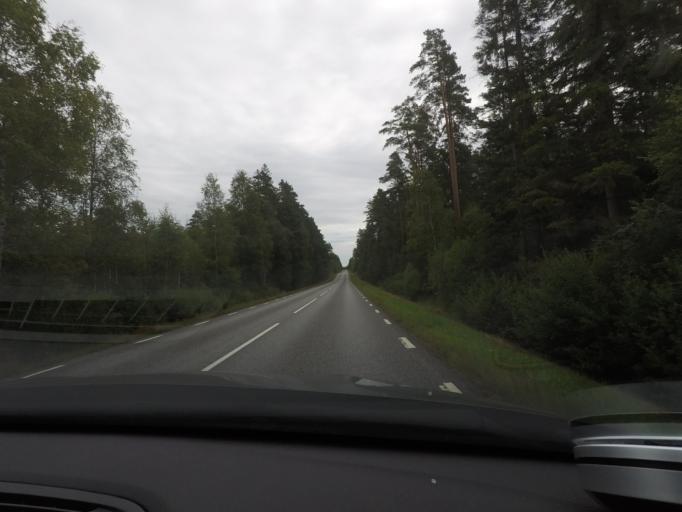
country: SE
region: Skane
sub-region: Osby Kommun
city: Lonsboda
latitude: 56.4379
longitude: 14.4811
